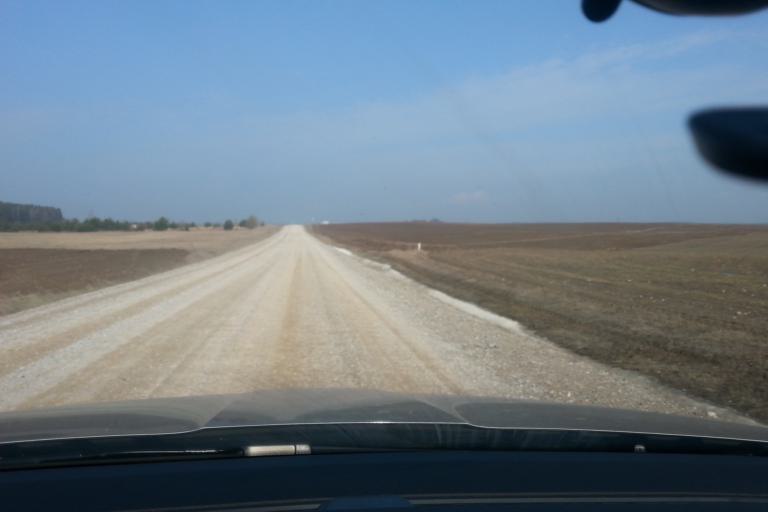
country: LT
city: Trakai
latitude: 54.5885
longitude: 24.9770
